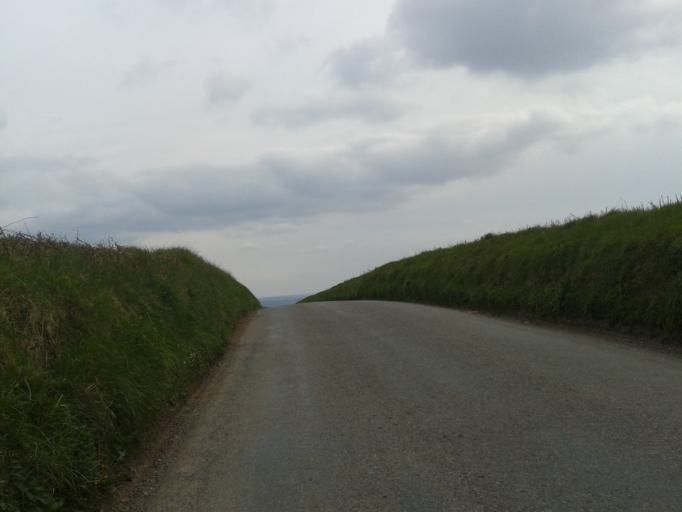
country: GB
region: England
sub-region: Devon
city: Braunton
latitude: 51.1485
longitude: -4.1912
